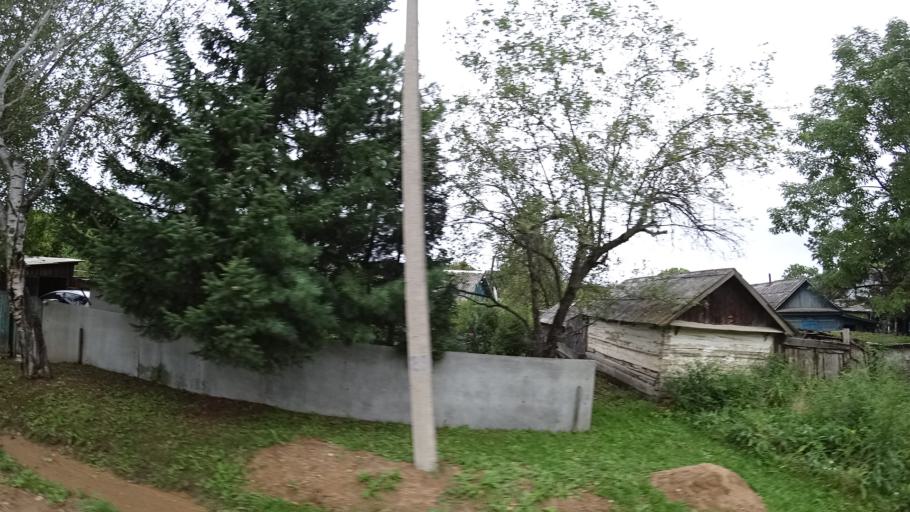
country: RU
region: Primorskiy
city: Rettikhovka
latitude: 44.1622
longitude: 132.7428
